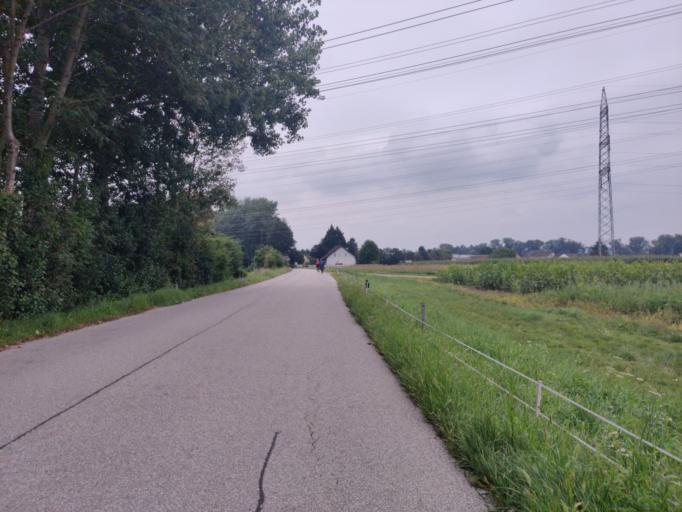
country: AT
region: Lower Austria
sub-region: Politischer Bezirk Tulln
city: Langenrohr
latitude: 48.3285
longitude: 16.0012
